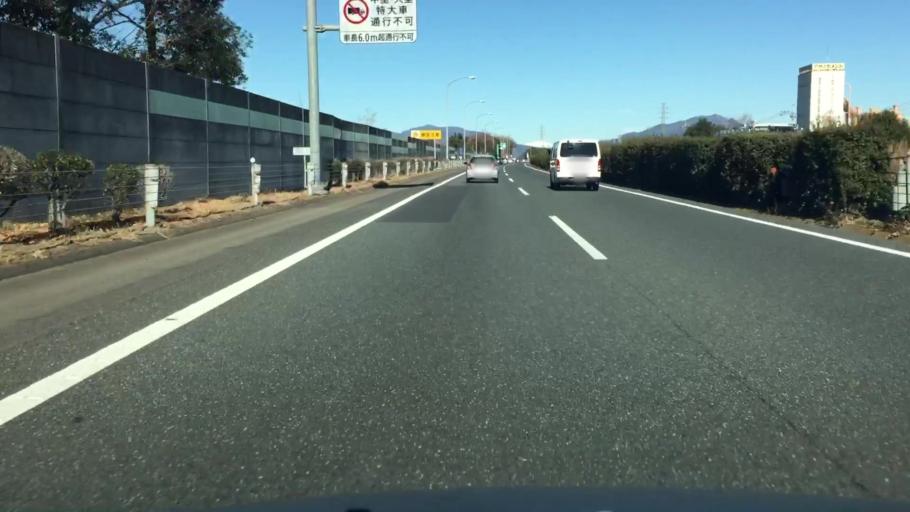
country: JP
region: Gunma
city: Kanekomachi
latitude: 36.4243
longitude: 139.0170
